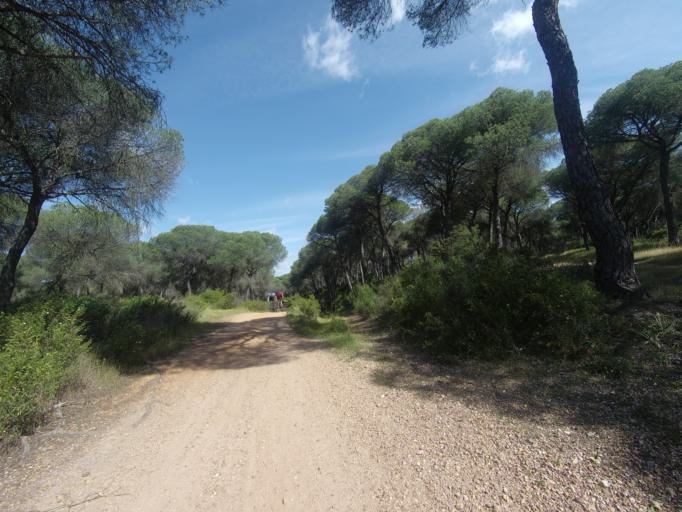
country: ES
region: Andalusia
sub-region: Provincia de Huelva
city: Aljaraque
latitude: 37.2334
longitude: -7.0497
